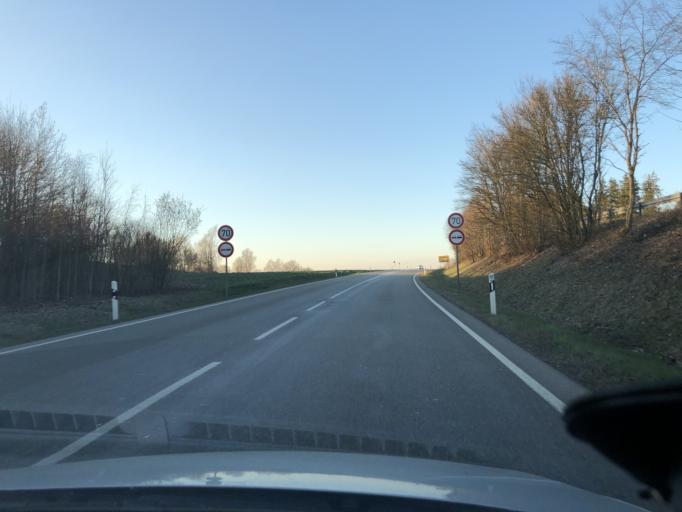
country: DE
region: Baden-Wuerttemberg
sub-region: Freiburg Region
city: Hufingen
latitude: 47.9143
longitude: 8.5041
